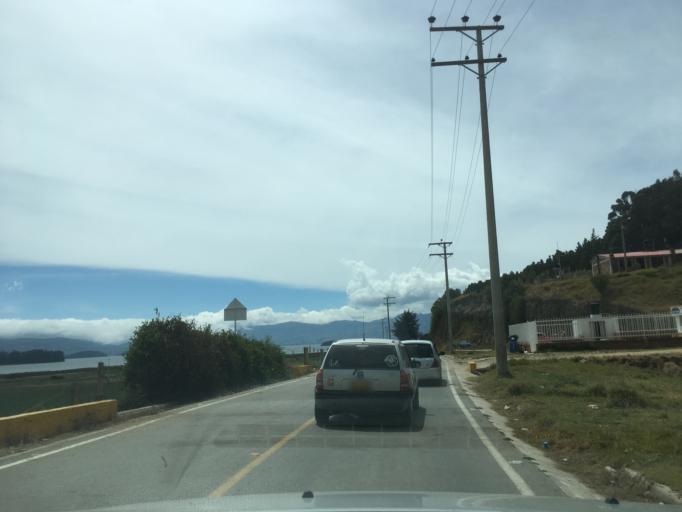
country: CO
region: Boyaca
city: Aquitania
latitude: 5.6007
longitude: -72.9129
